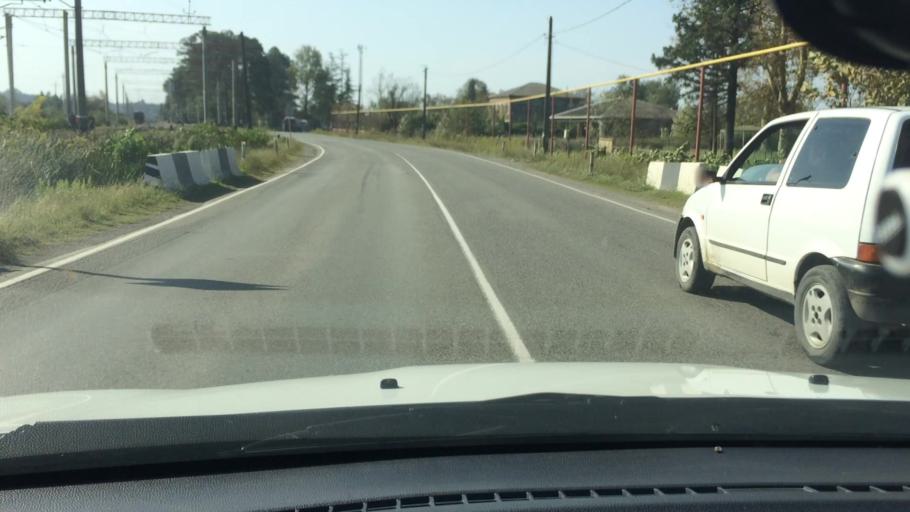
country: GE
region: Guria
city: Urek'i
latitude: 42.0453
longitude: 41.8144
